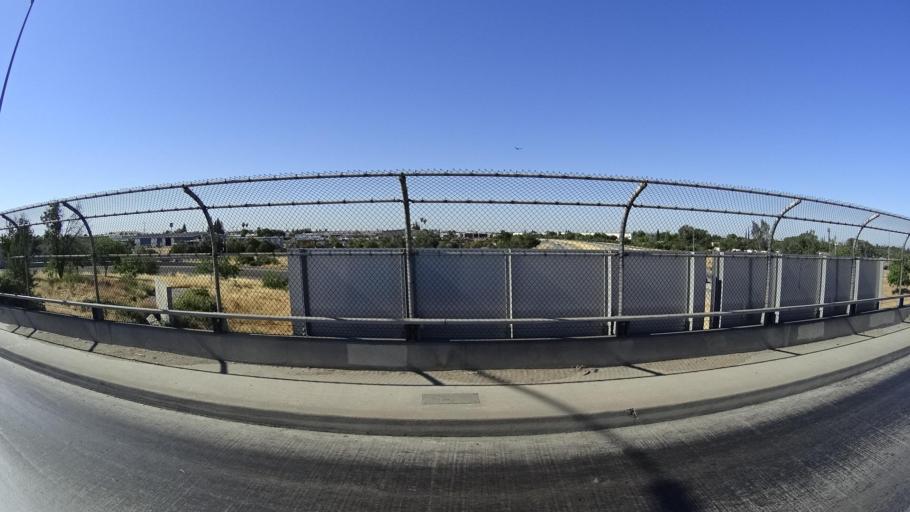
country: US
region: California
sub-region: Fresno County
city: Fresno
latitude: 36.7065
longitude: -119.7853
